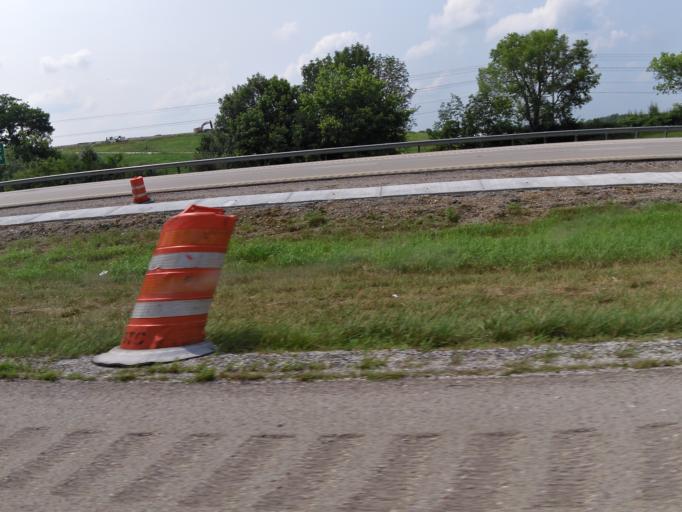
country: US
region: Kentucky
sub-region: Boone County
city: Verona
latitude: 38.8595
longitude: -84.6565
